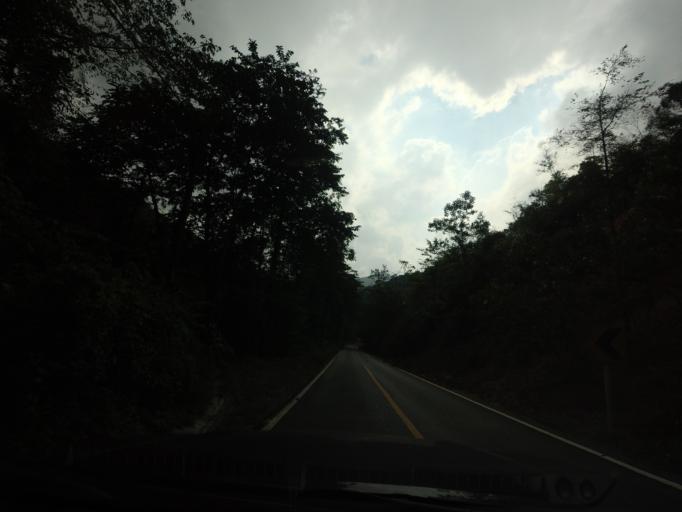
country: TH
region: Nan
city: Bo Kluea
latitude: 19.1929
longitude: 101.0782
